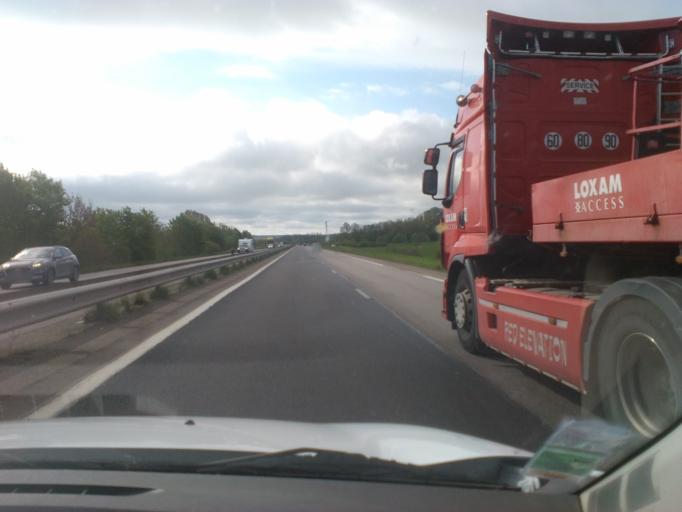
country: FR
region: Lorraine
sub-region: Departement des Vosges
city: Vincey
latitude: 48.3399
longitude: 6.3151
